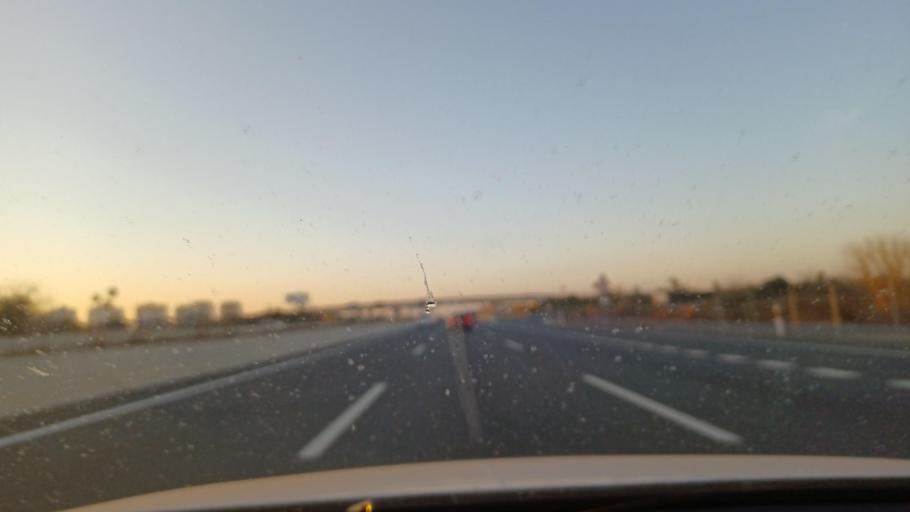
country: ES
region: Valencia
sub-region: Provincia de Valencia
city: Puig
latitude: 39.5704
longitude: -0.2957
